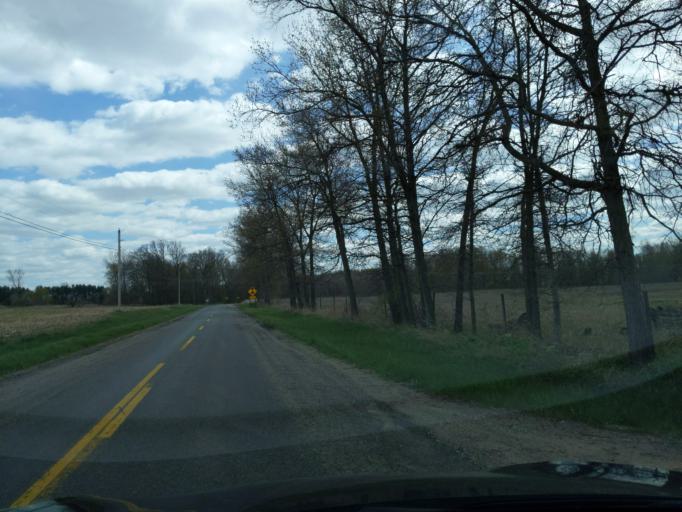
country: US
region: Michigan
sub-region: Eaton County
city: Eaton Rapids
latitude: 42.5116
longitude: -84.5420
